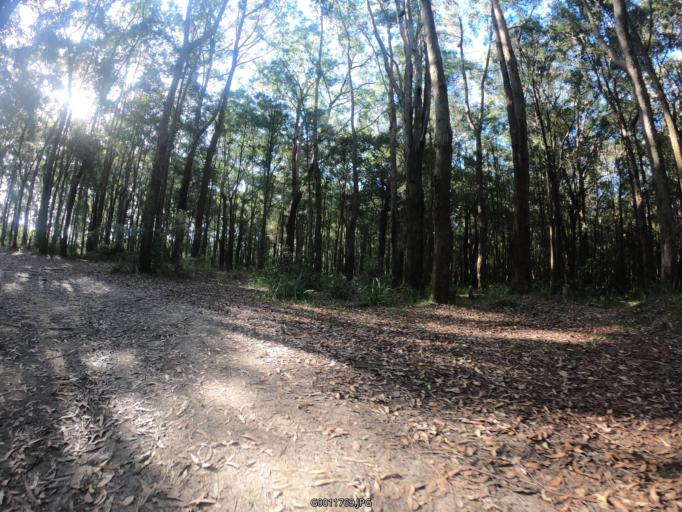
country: AU
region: New South Wales
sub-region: Lake Macquarie Shire
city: Cooranbong
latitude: -33.0620
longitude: 151.3322
